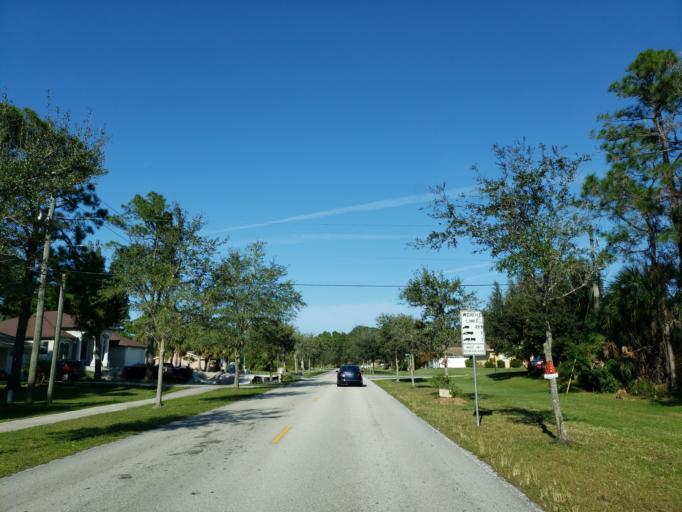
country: US
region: Florida
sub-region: Sarasota County
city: North Port
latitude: 27.0730
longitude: -82.1962
